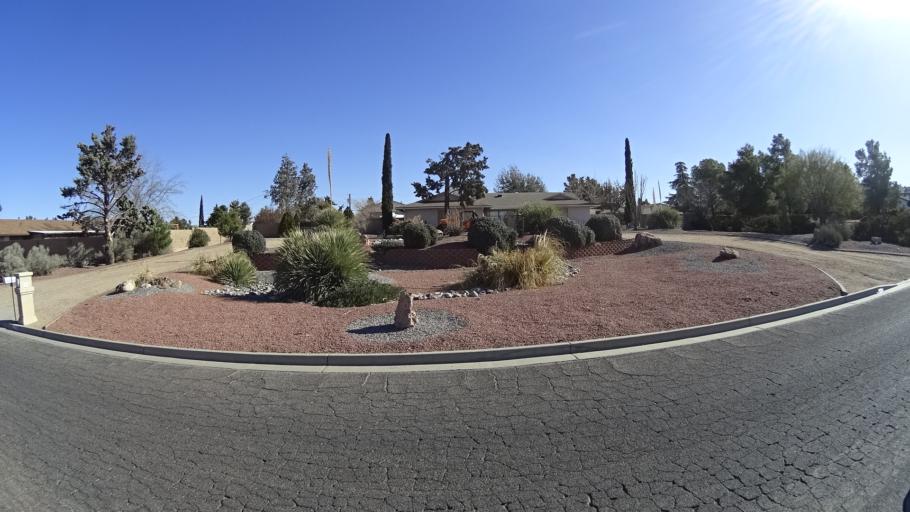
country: US
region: Arizona
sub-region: Mohave County
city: Kingman
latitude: 35.1999
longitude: -114.0075
